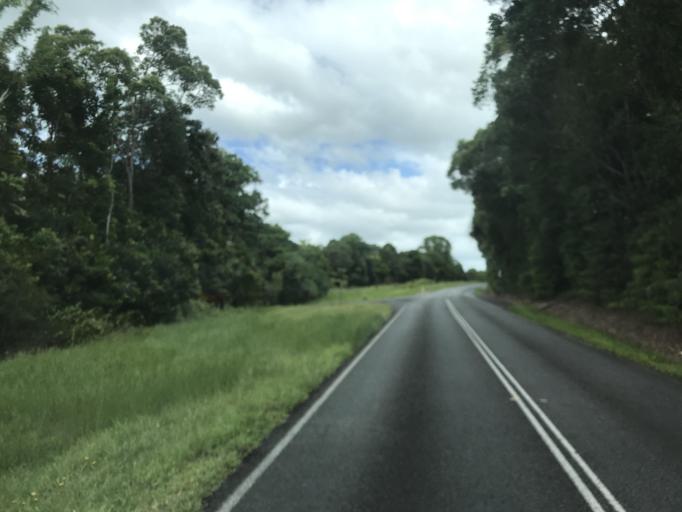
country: AU
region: Queensland
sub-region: Cassowary Coast
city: Innisfail
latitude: -17.8383
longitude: 146.0527
